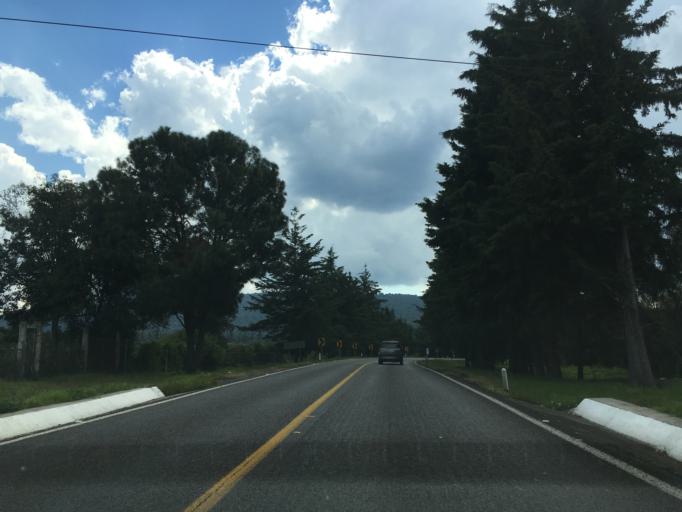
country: MX
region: Michoacan
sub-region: Patzcuaro
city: Santa Ana Chapitiro
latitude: 19.5147
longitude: -101.6675
